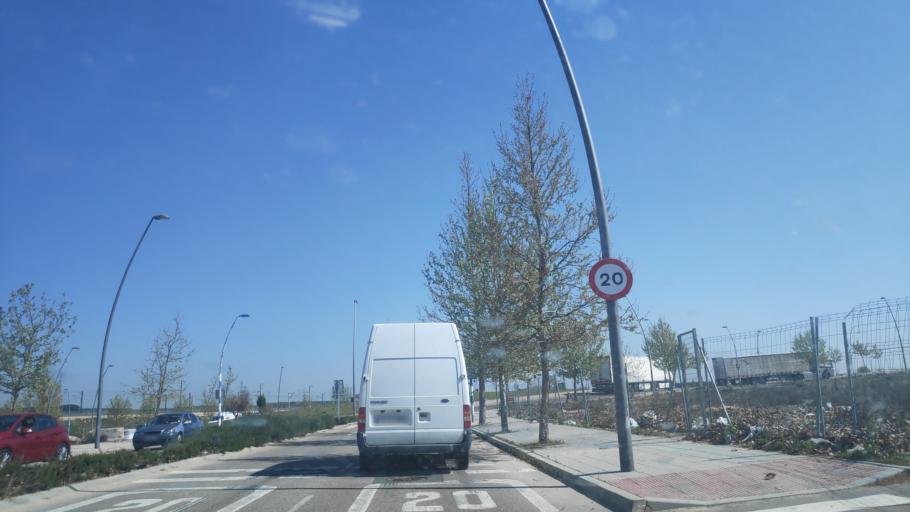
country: ES
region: Madrid
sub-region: Provincia de Madrid
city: Pinto
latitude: 40.2885
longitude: -3.6813
